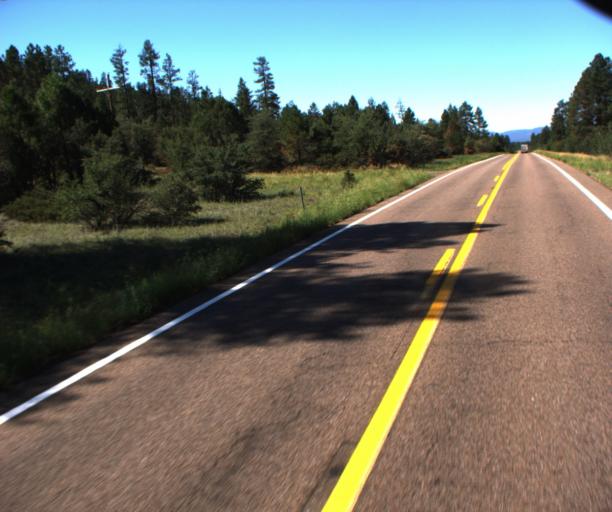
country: US
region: Arizona
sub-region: Navajo County
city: Linden
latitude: 34.0826
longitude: -110.1858
